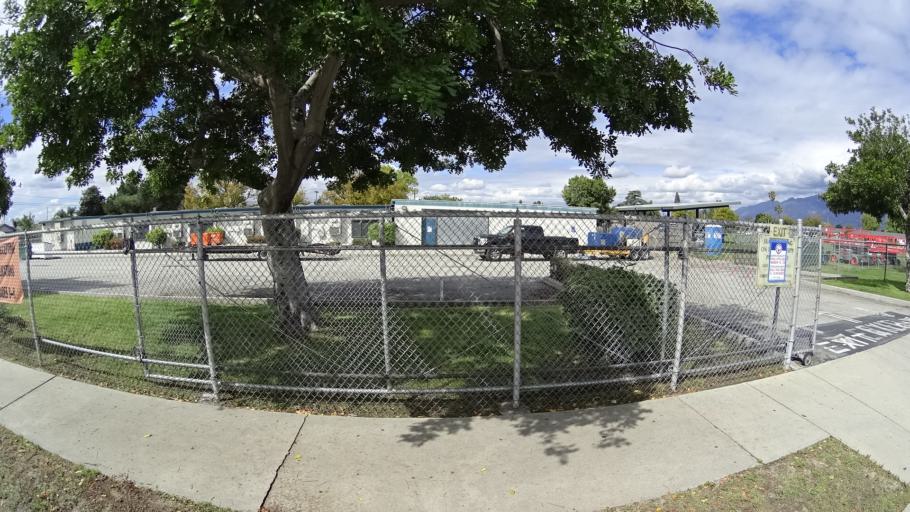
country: US
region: California
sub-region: Los Angeles County
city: Baldwin Park
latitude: 34.0964
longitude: -117.9633
